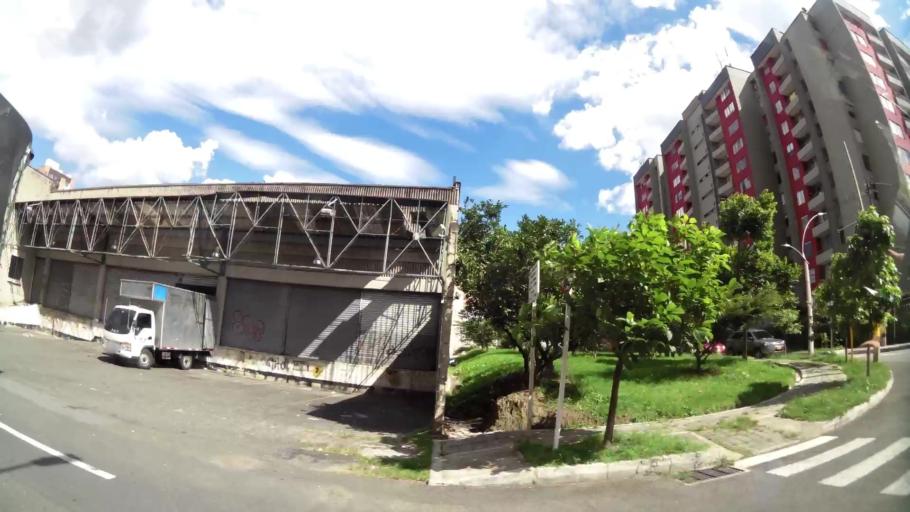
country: CO
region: Antioquia
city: Sabaneta
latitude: 6.1564
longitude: -75.6090
